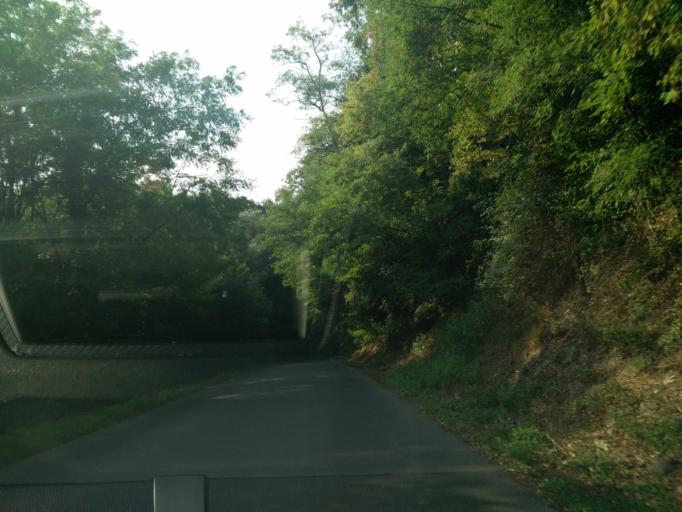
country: SK
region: Banskobystricky
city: Zarnovica
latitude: 48.5166
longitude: 18.7720
